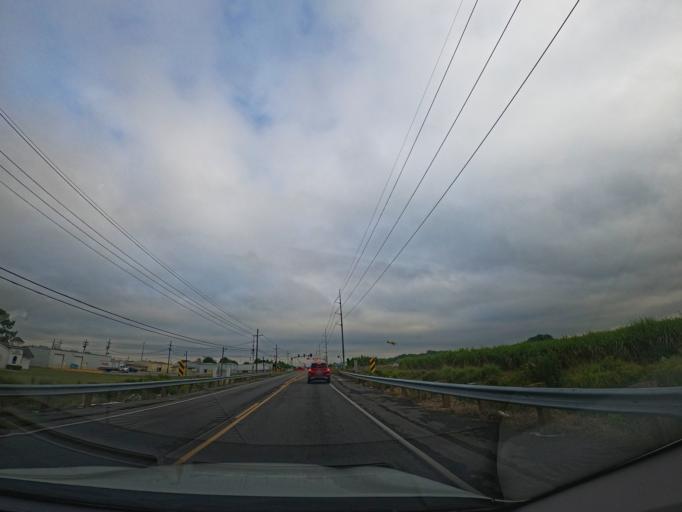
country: US
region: Louisiana
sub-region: Terrebonne Parish
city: Presquille
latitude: 29.5442
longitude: -90.6783
